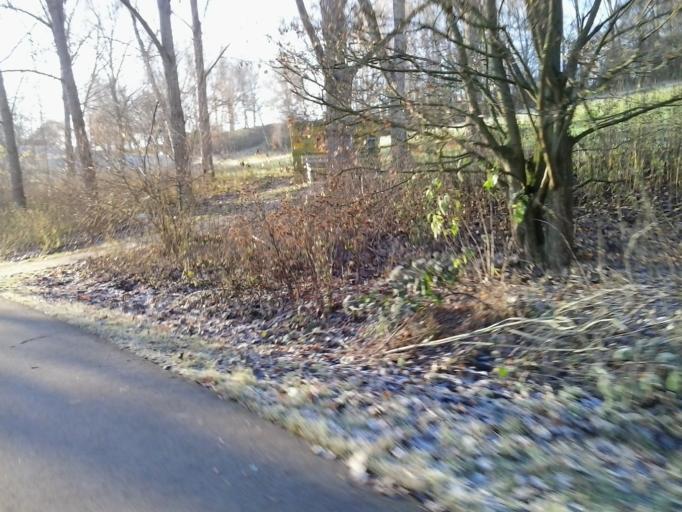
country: NL
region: South Holland
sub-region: Gemeente Lansingerland
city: Bergschenhoek
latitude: 51.9720
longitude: 4.5266
